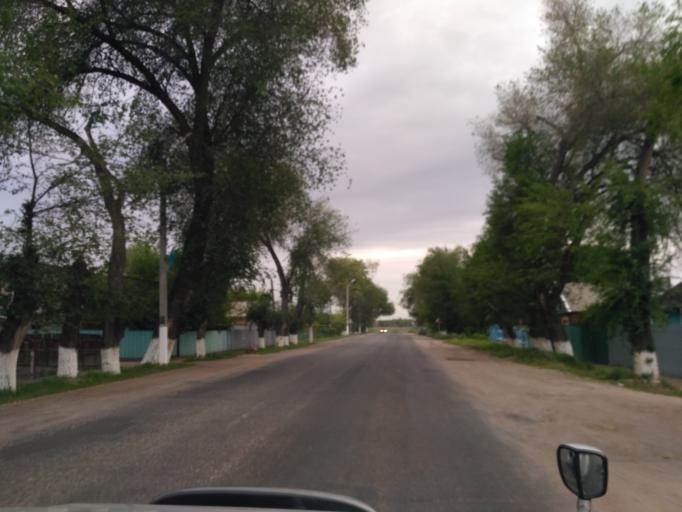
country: KZ
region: Almaty Oblysy
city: Burunday
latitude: 43.4607
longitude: 76.7238
